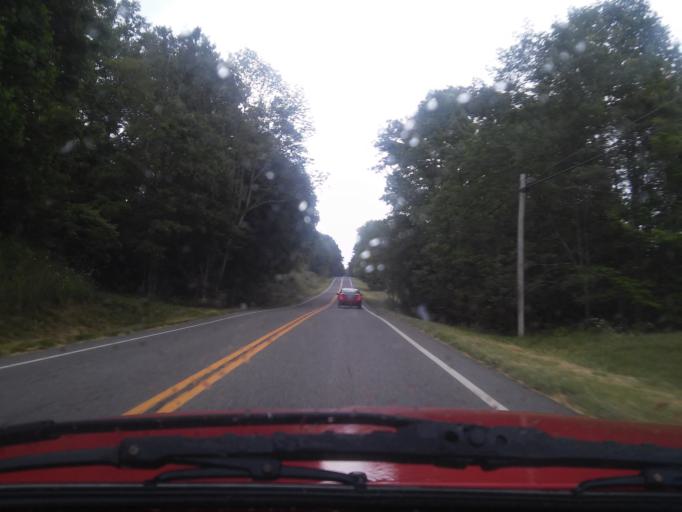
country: US
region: Virginia
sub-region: Montgomery County
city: Blacksburg
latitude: 37.3179
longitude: -80.4621
